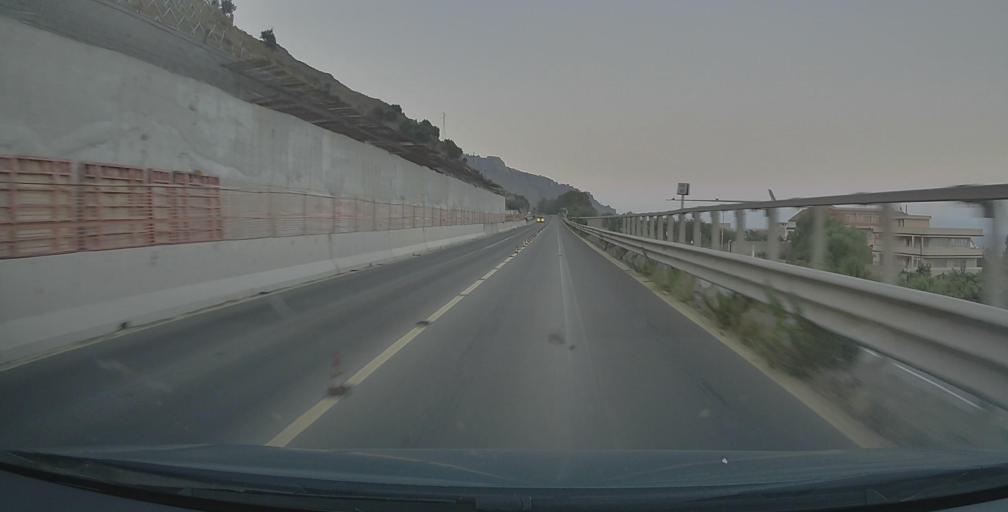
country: IT
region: Sicily
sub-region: Messina
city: Letojanni
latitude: 37.8913
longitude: 15.3186
